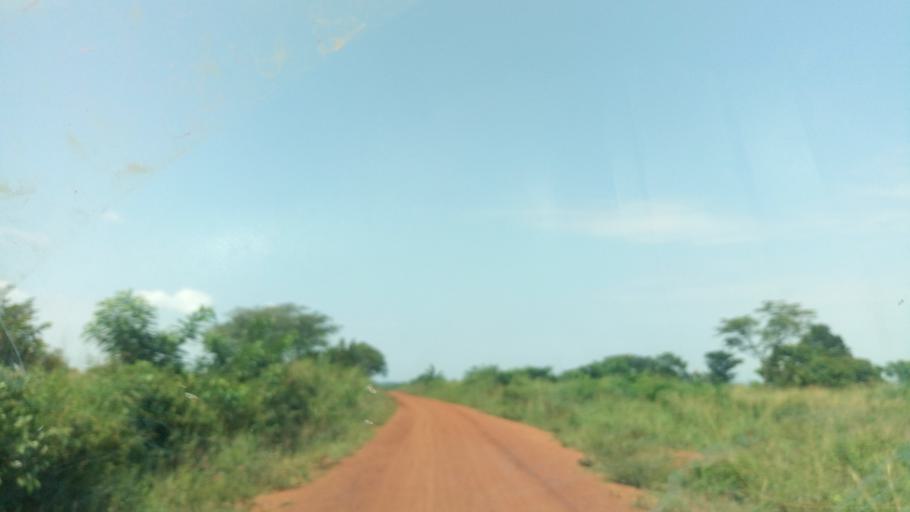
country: UG
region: Western Region
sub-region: Masindi District
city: Masindi
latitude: 1.6818
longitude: 31.8314
